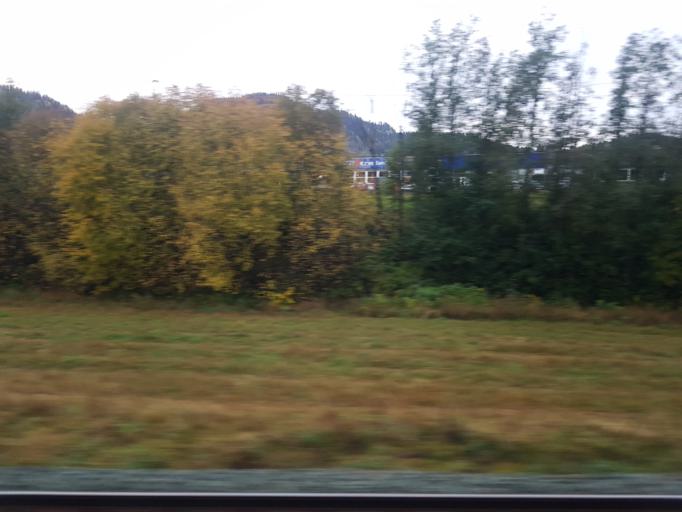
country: NO
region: Sor-Trondelag
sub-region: Melhus
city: Lundamo
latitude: 63.1328
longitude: 10.2564
